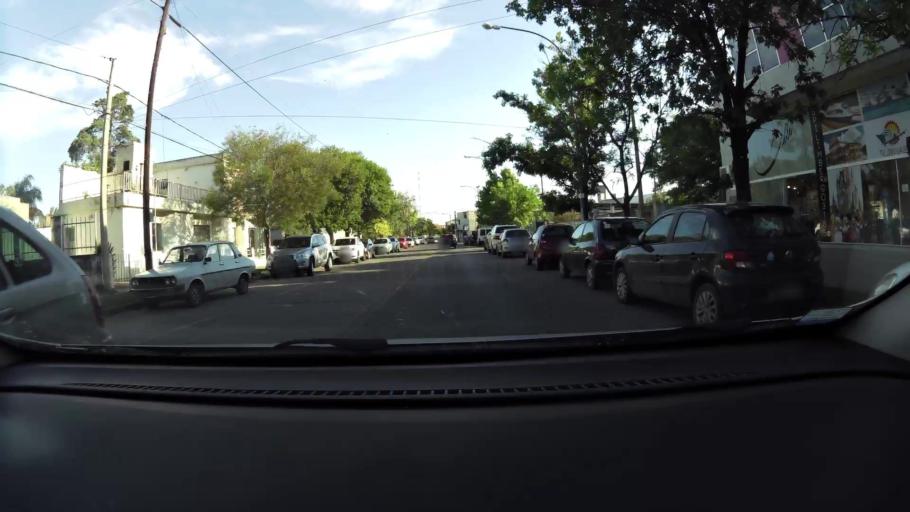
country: AR
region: Cordoba
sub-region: Departamento de Capital
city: Cordoba
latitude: -31.3721
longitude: -64.2265
